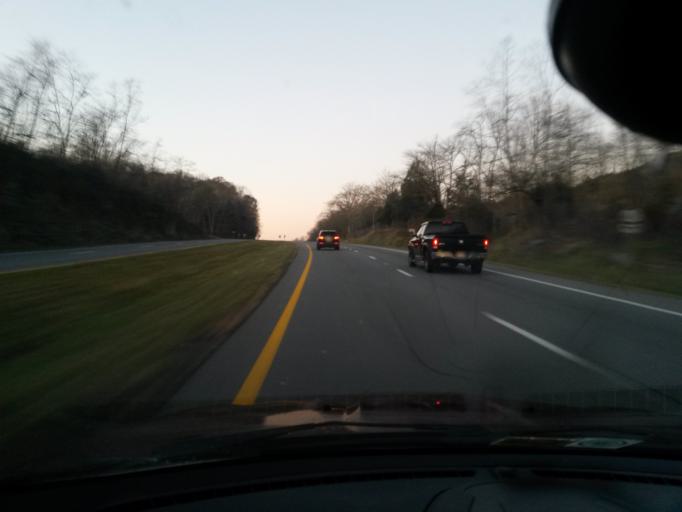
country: US
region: Virginia
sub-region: Botetourt County
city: Fincastle
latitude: 37.6348
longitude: -79.8085
